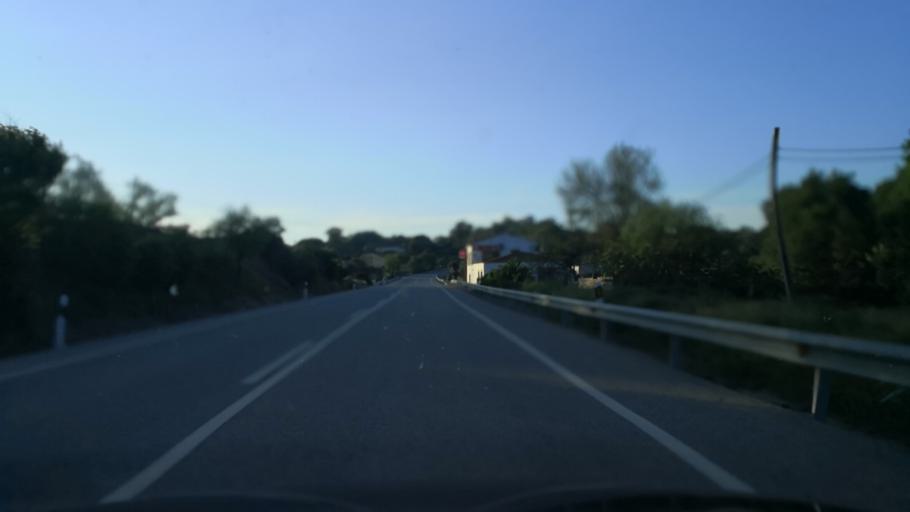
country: ES
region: Extremadura
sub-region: Provincia de Caceres
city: Valencia de Alcantara
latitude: 39.3974
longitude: -7.2494
